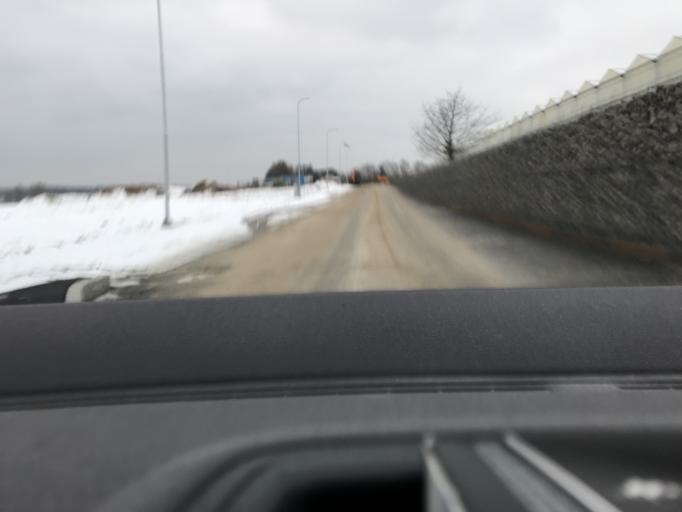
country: SE
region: Skane
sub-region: Ystads Kommun
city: Ystad
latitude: 55.4517
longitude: 13.8548
